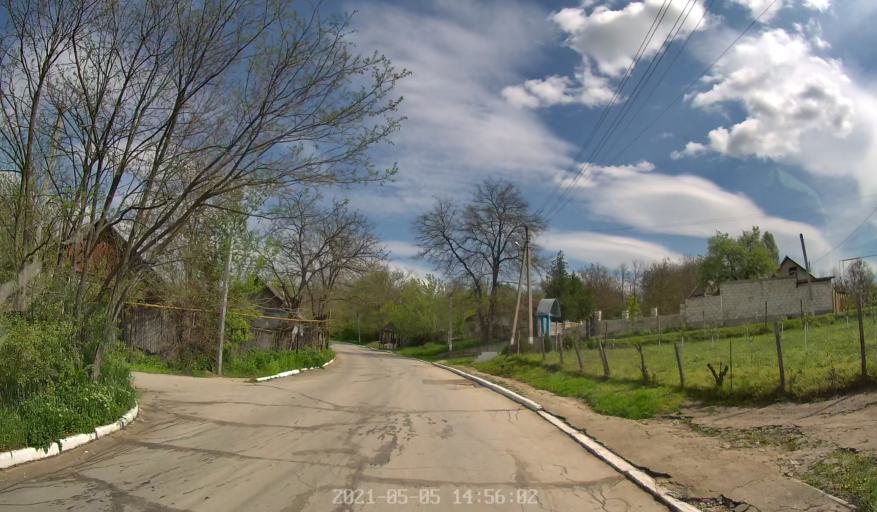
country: MD
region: Chisinau
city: Vadul lui Voda
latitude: 47.0987
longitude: 29.1734
